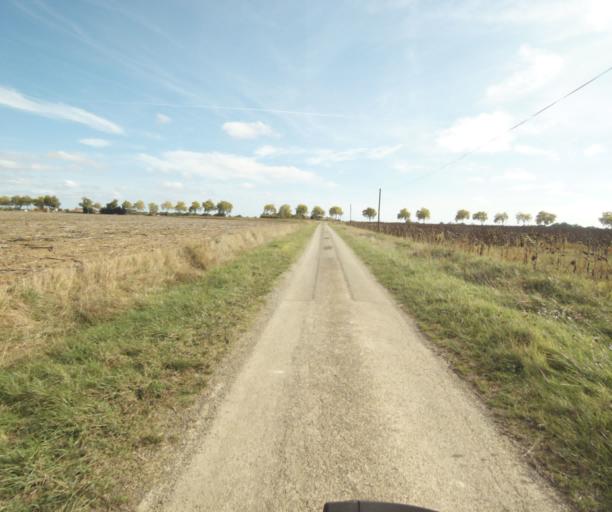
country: FR
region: Midi-Pyrenees
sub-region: Departement du Tarn-et-Garonne
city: Saint-Porquier
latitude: 43.9474
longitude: 1.1419
